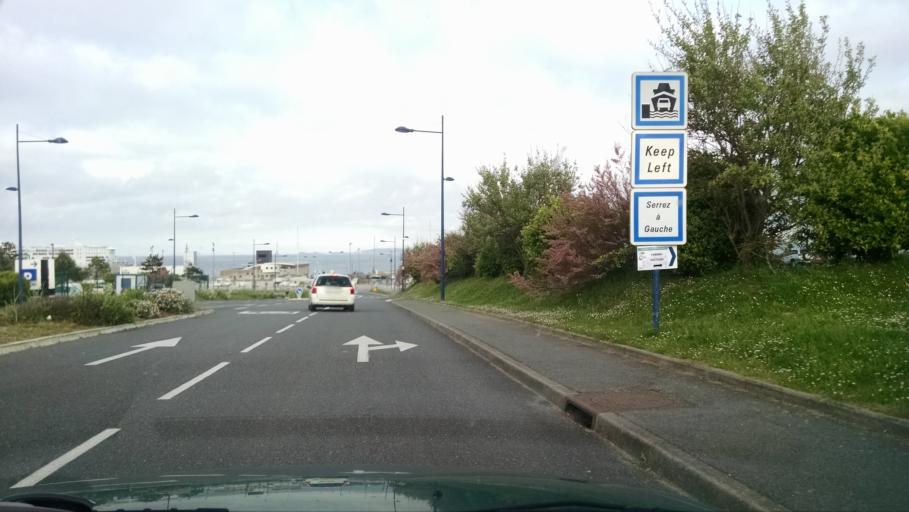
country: FR
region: Brittany
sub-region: Departement du Finistere
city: Roscoff
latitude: 48.7196
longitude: -3.9711
